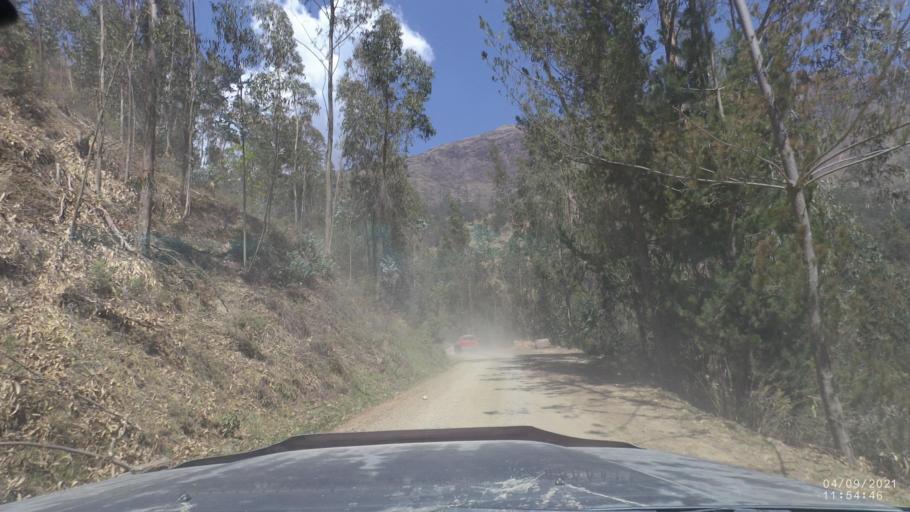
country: BO
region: Cochabamba
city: Colchani
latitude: -17.2386
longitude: -66.5250
